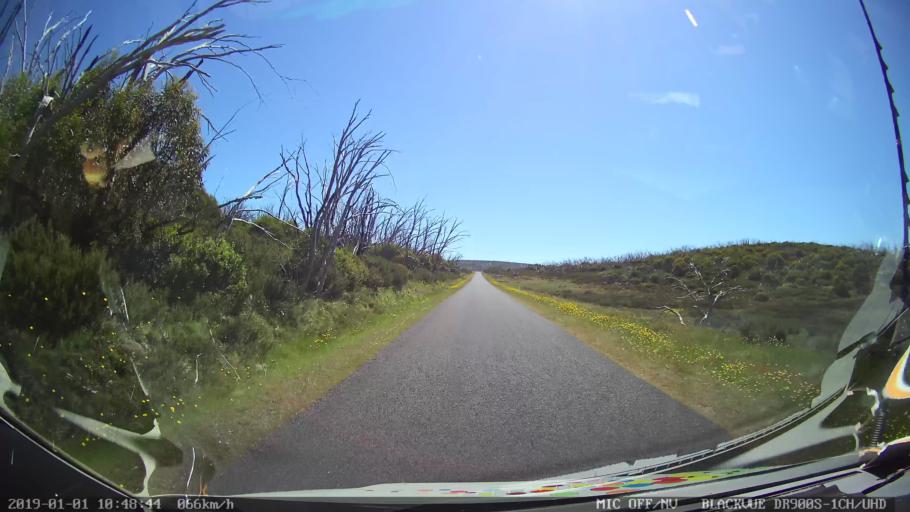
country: AU
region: New South Wales
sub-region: Snowy River
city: Jindabyne
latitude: -36.0381
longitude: 148.3634
